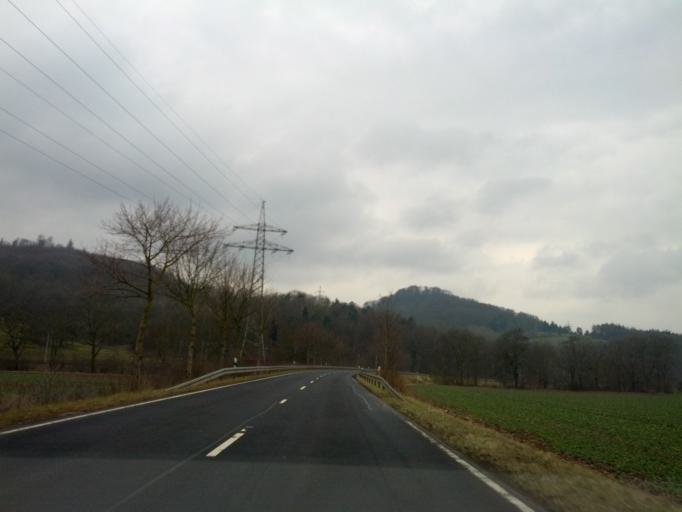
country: DE
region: Thuringia
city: Krauthausen
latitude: 50.9882
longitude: 10.2600
